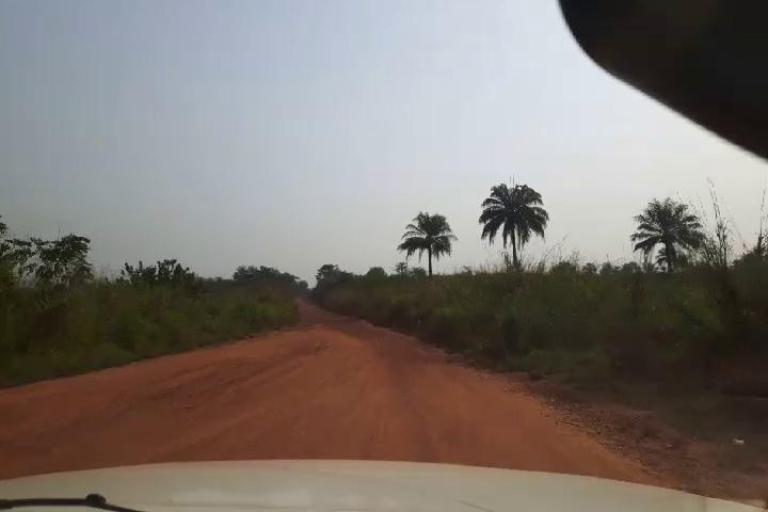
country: SL
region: Northern Province
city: Masingbi
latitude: 8.8299
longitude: -11.8501
